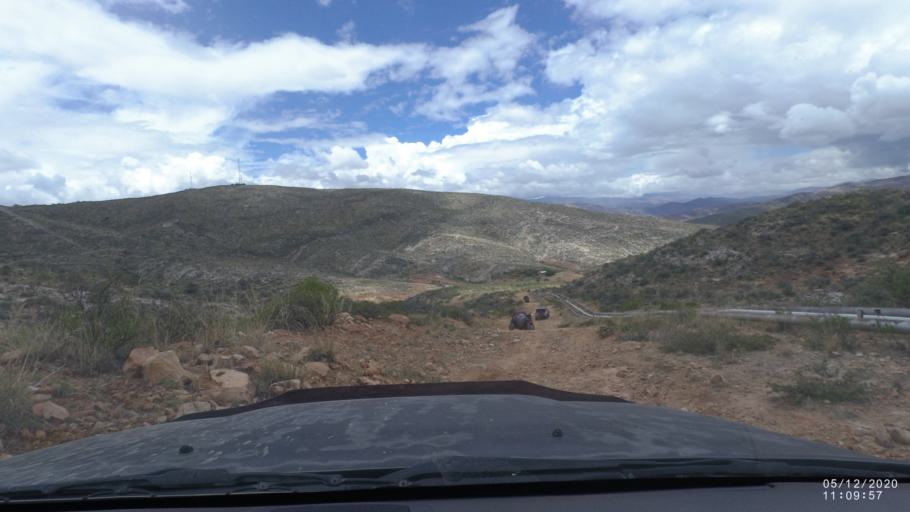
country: BO
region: Cochabamba
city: Sipe Sipe
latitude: -17.5499
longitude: -66.3187
